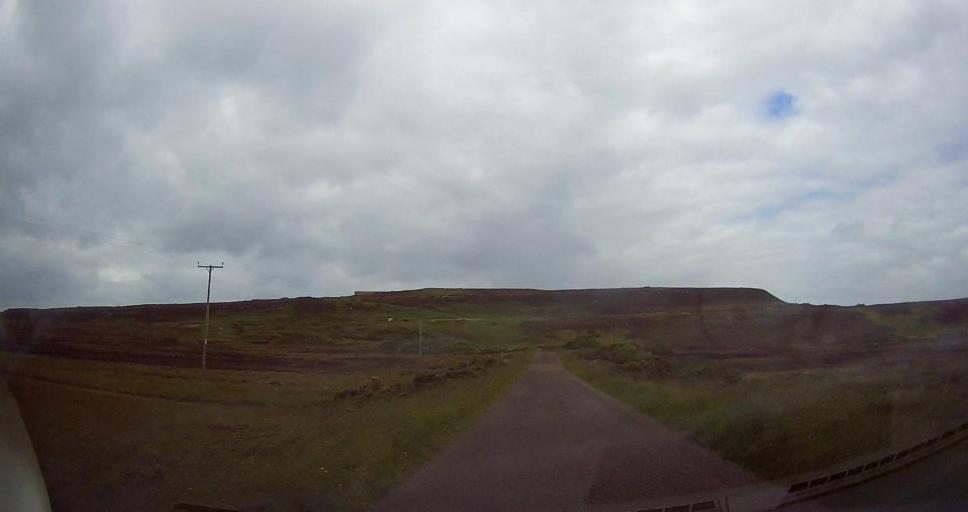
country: GB
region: Scotland
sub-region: Highland
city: Thurso
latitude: 58.6557
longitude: -3.3709
